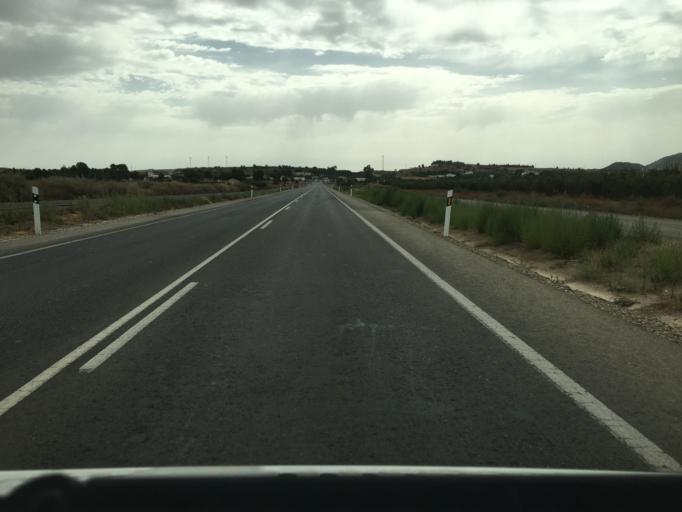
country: ES
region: Andalusia
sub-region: Provincia de Almeria
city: Huercal-Overa
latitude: 37.4172
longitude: -1.8858
